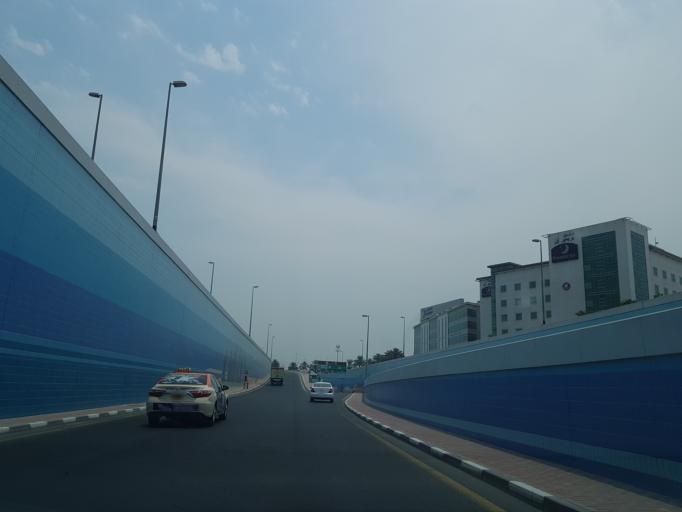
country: AE
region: Ash Shariqah
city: Sharjah
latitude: 25.2440
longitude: 55.3582
